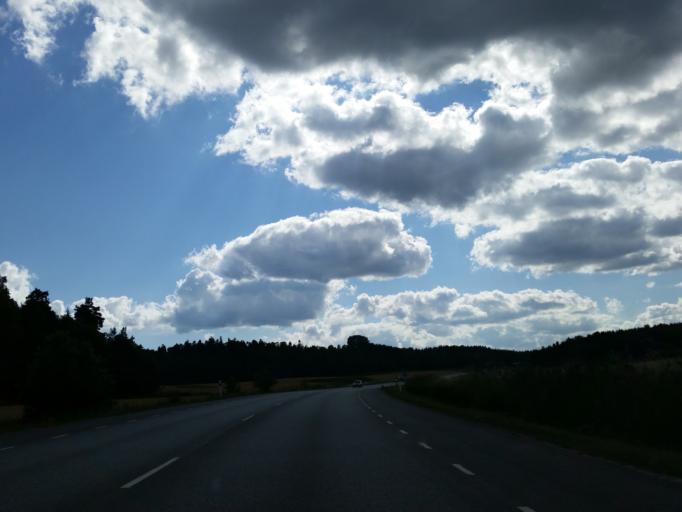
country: SE
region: Soedermanland
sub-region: Trosa Kommun
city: Vagnharad
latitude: 58.9509
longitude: 17.5471
